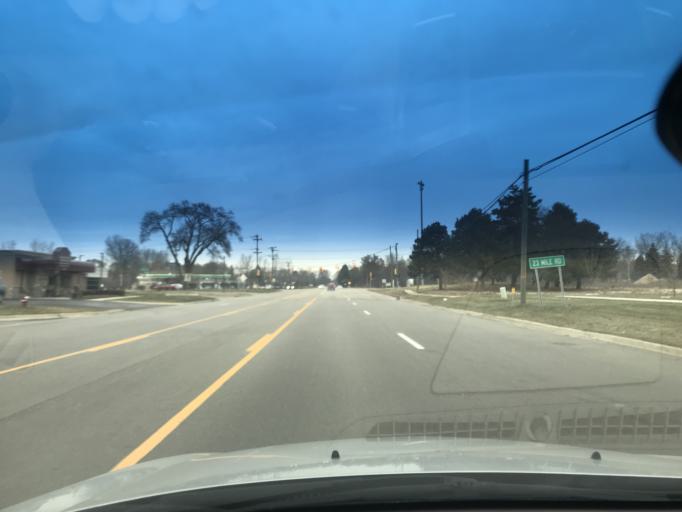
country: US
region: Michigan
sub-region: Macomb County
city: Shelby
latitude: 42.6677
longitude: -83.0535
